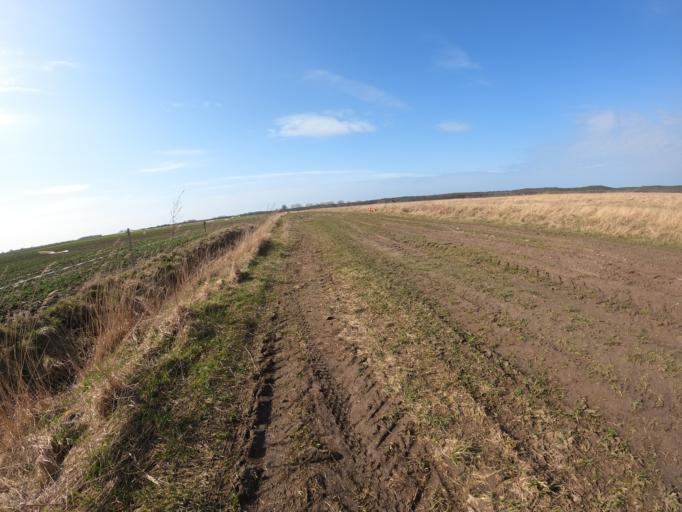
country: PL
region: West Pomeranian Voivodeship
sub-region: Powiat gryficki
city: Trzebiatow
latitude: 54.0936
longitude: 15.2012
